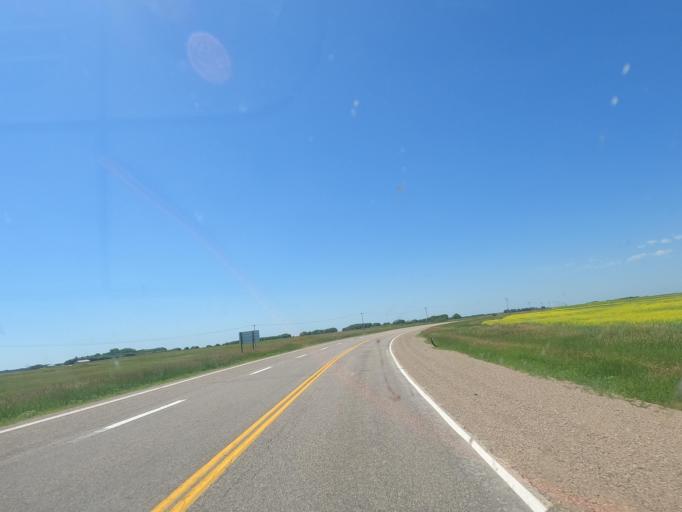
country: CA
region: Manitoba
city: Souris
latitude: 49.5857
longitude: -100.5349
